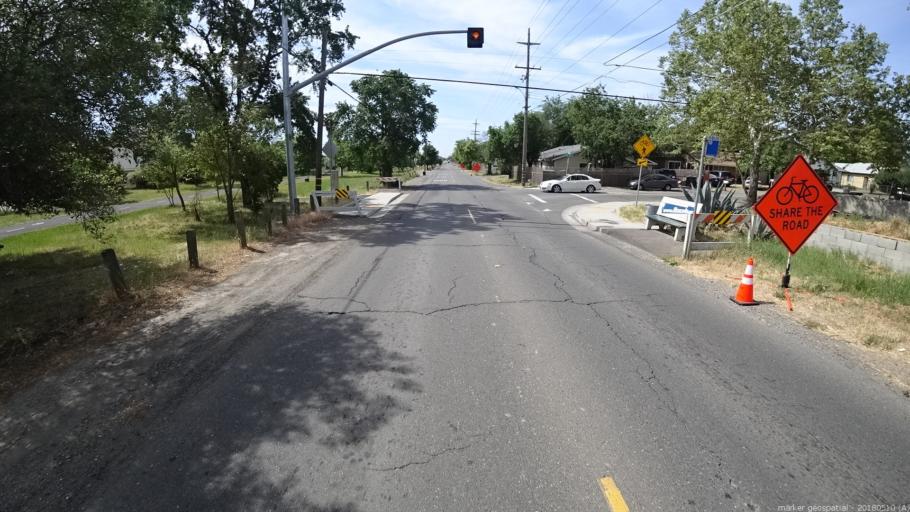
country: US
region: California
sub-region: Sacramento County
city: Rio Linda
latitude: 38.6586
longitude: -121.4477
